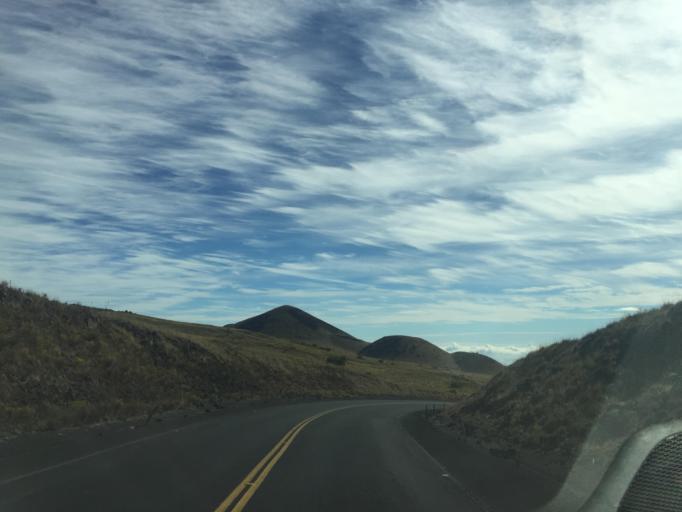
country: US
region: Hawaii
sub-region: Hawaii County
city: Volcano
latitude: 19.7217
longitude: -155.4475
